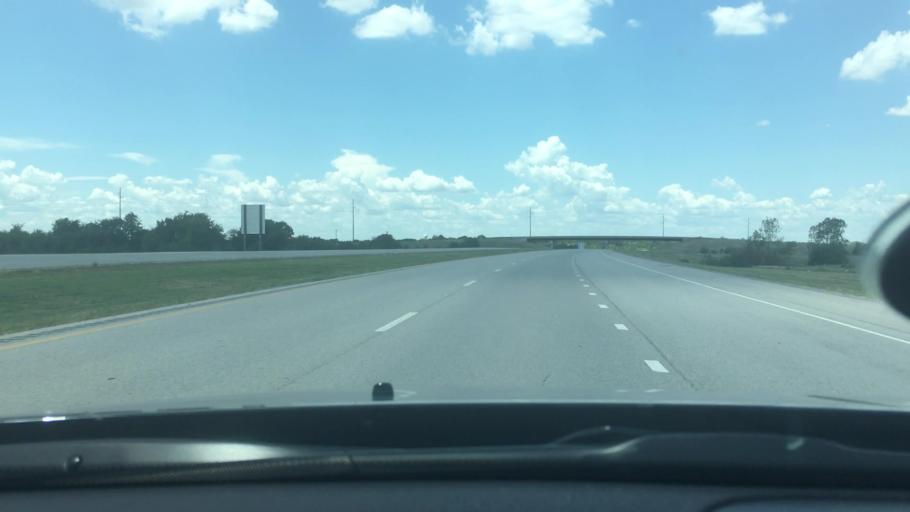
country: US
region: Oklahoma
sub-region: Bryan County
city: Calera
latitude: 33.9728
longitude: -96.4214
